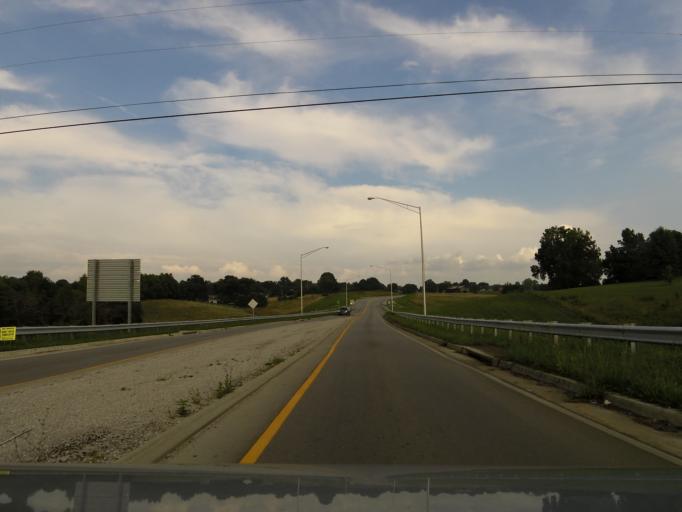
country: US
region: Kentucky
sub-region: Harrison County
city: Cynthiana
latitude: 38.3684
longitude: -84.3195
